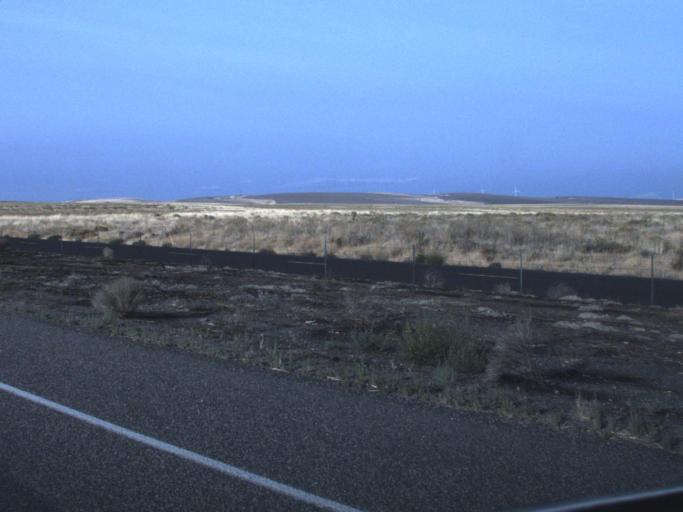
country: US
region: Washington
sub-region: Benton County
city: Highland
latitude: 46.0332
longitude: -119.2244
